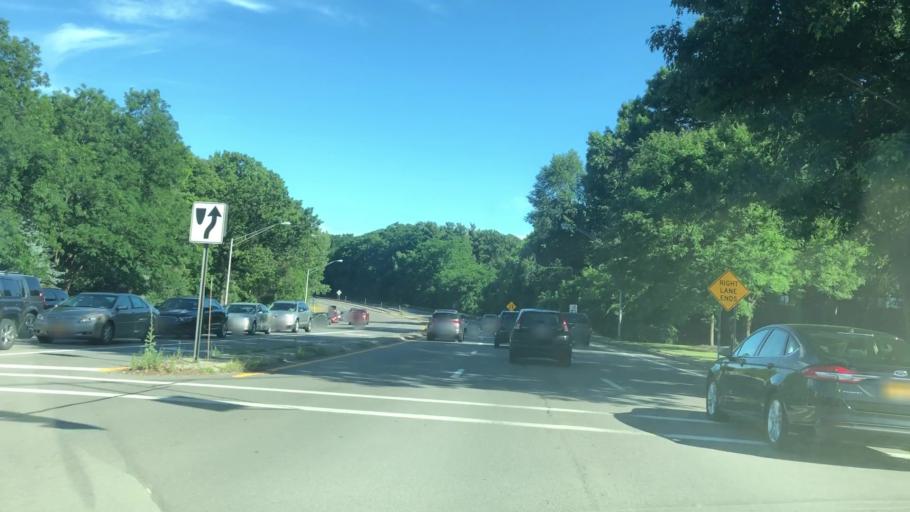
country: US
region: New York
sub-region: Monroe County
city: Pittsford
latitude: 43.1262
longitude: -77.5201
